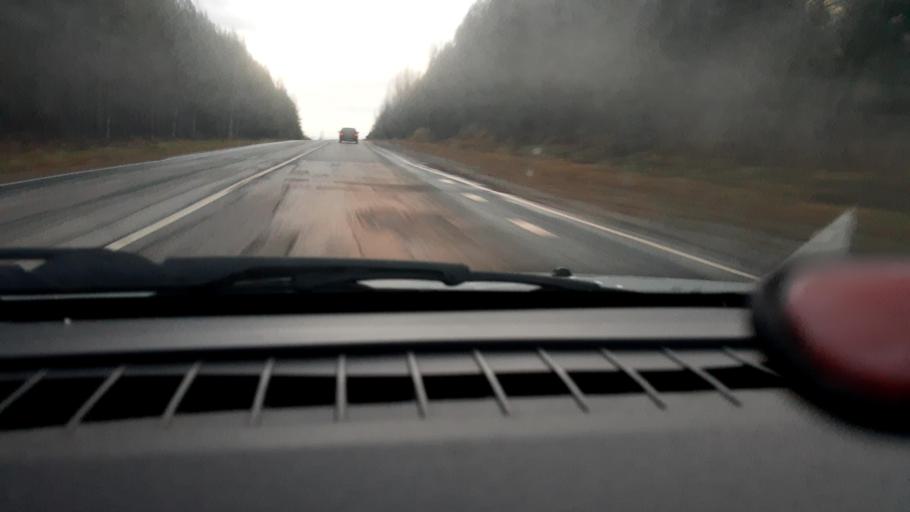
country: RU
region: Nizjnij Novgorod
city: Vladimirskoye
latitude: 56.9685
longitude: 45.1105
